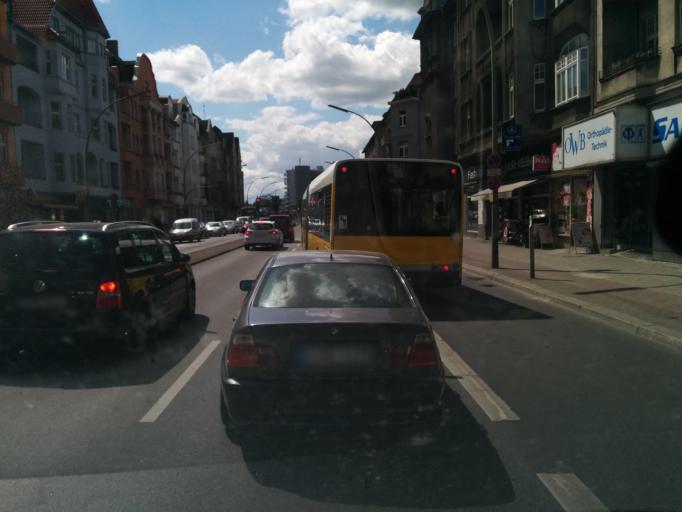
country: DE
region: Berlin
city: Spandau
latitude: 52.5318
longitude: 13.1973
